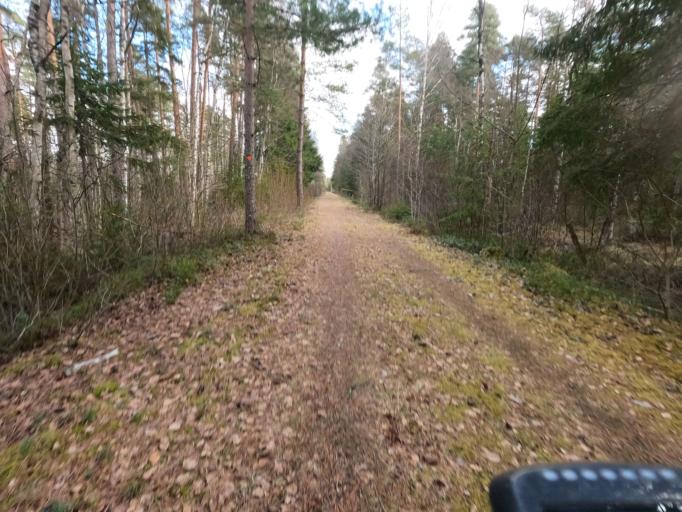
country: SE
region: Joenkoeping
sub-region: Varnamo Kommun
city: Rydaholm
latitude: 56.8234
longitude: 14.2947
